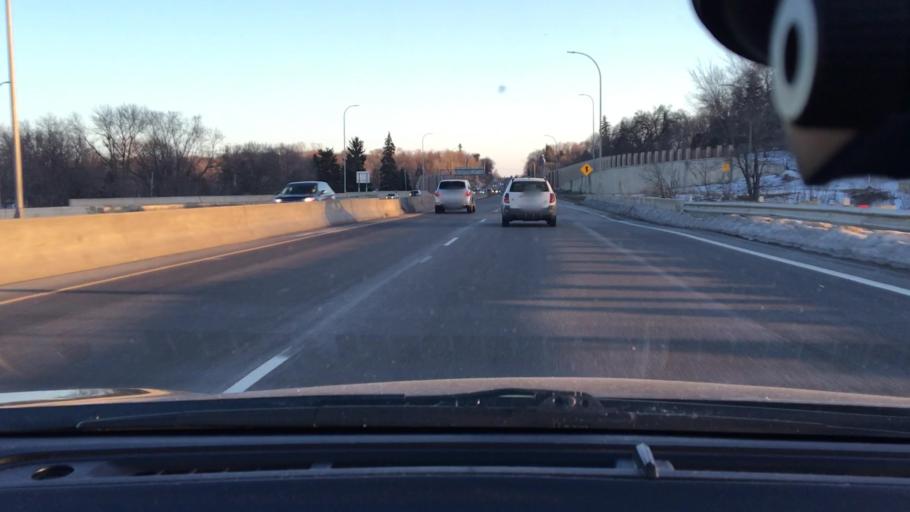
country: US
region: Minnesota
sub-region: Hennepin County
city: Minnetonka Mills
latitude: 44.9721
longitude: -93.4007
